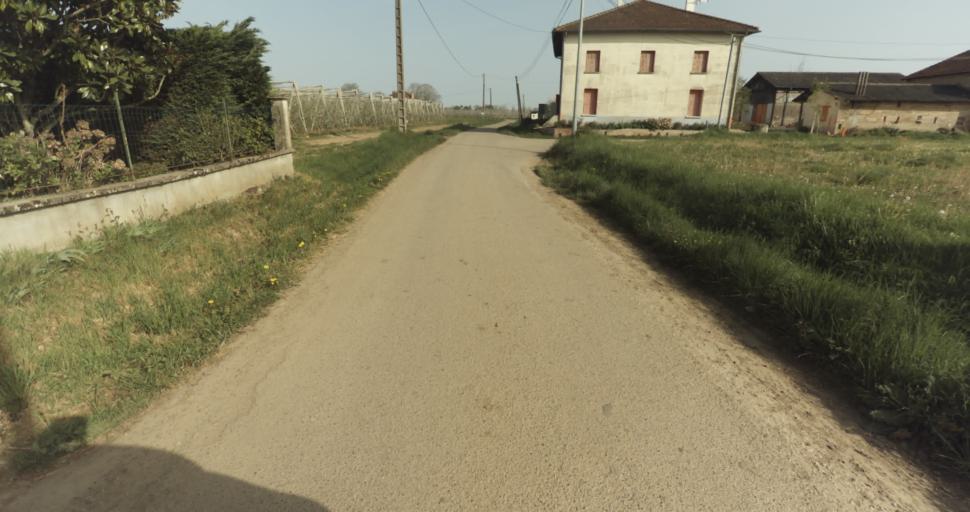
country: FR
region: Midi-Pyrenees
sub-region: Departement du Tarn-et-Garonne
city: Moissac
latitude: 44.1032
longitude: 1.1355
